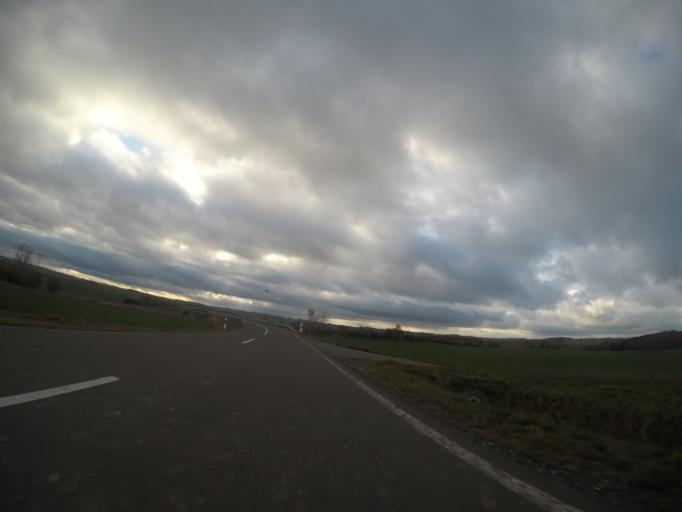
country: DE
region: Thuringia
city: Nobdenitz
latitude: 50.8646
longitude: 12.2885
